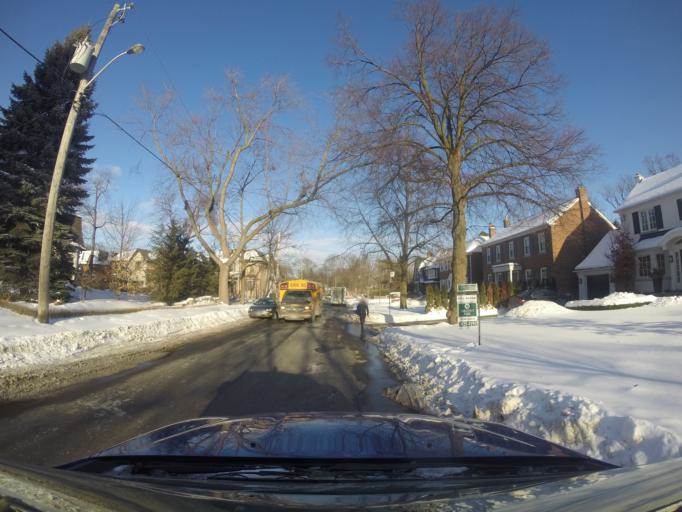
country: CA
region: Ontario
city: Toronto
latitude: 43.7253
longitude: -79.3816
